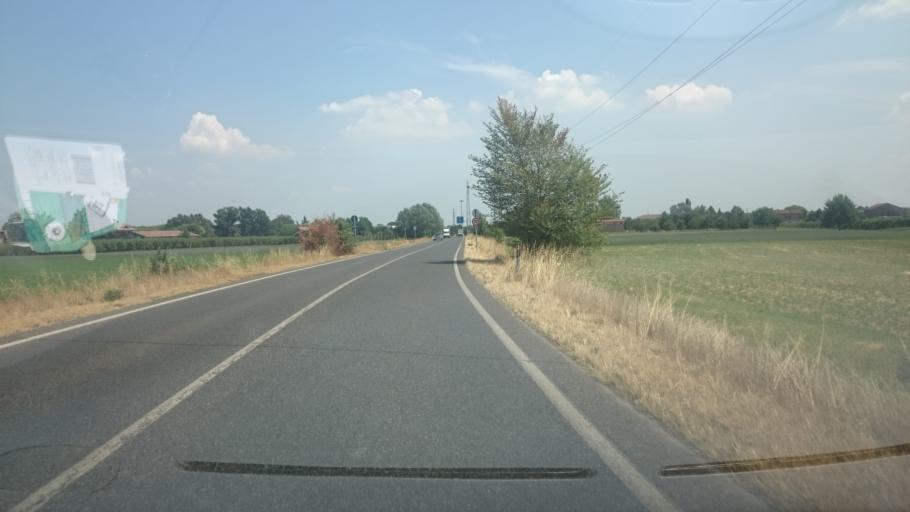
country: IT
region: Emilia-Romagna
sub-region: Provincia di Reggio Emilia
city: Arceto
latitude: 44.6292
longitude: 10.7213
